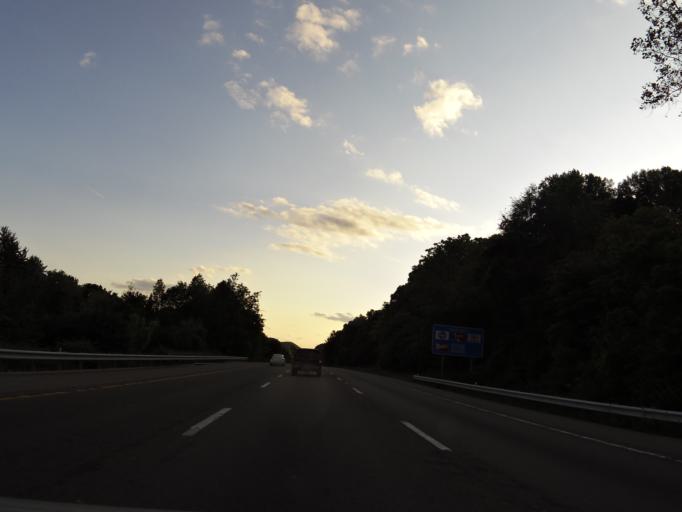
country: US
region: Virginia
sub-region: City of Bristol
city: Bristol
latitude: 36.6135
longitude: -82.2048
